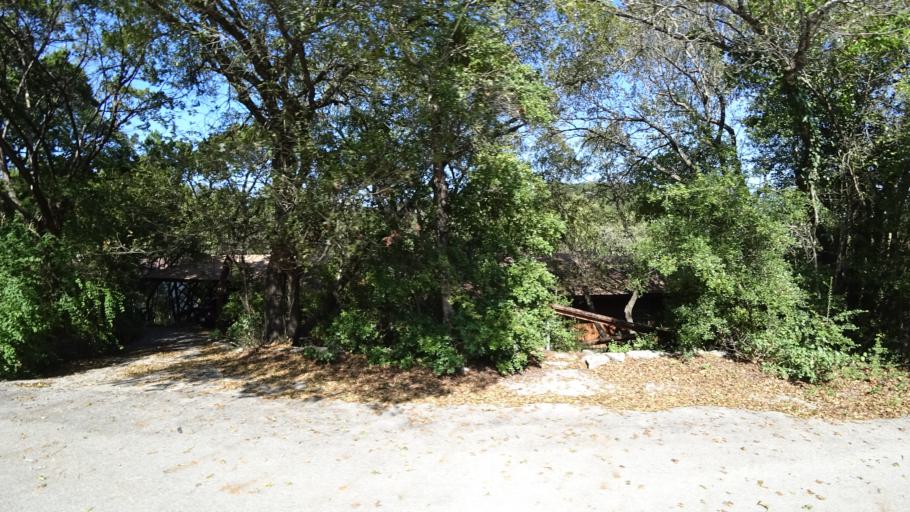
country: US
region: Texas
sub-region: Travis County
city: West Lake Hills
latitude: 30.2927
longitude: -97.8034
